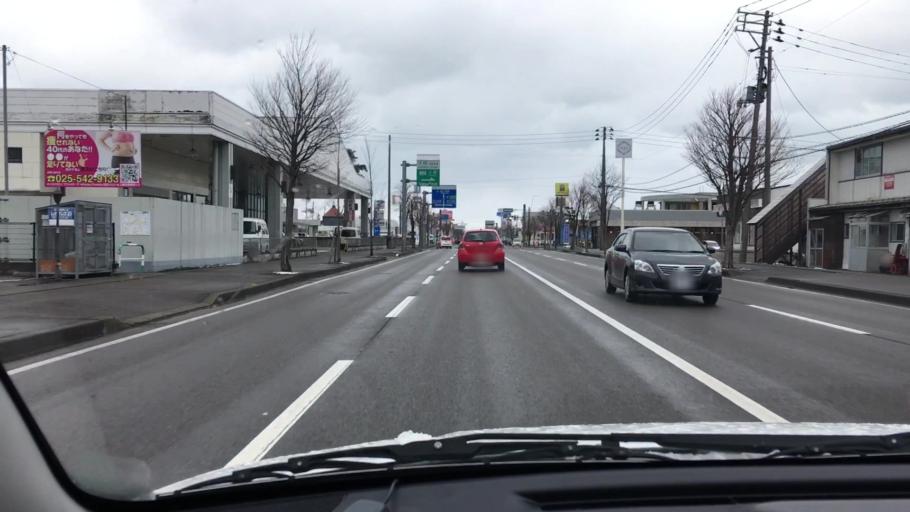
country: JP
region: Niigata
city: Joetsu
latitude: 37.1460
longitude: 138.2284
